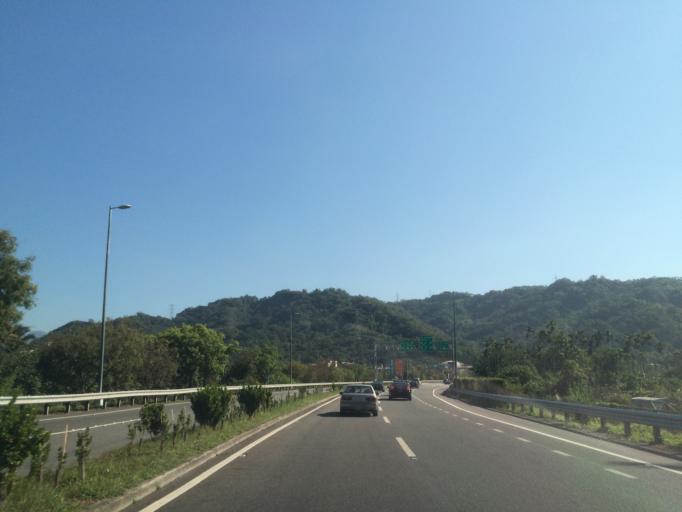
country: TW
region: Taiwan
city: Lugu
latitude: 23.7965
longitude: 120.7056
